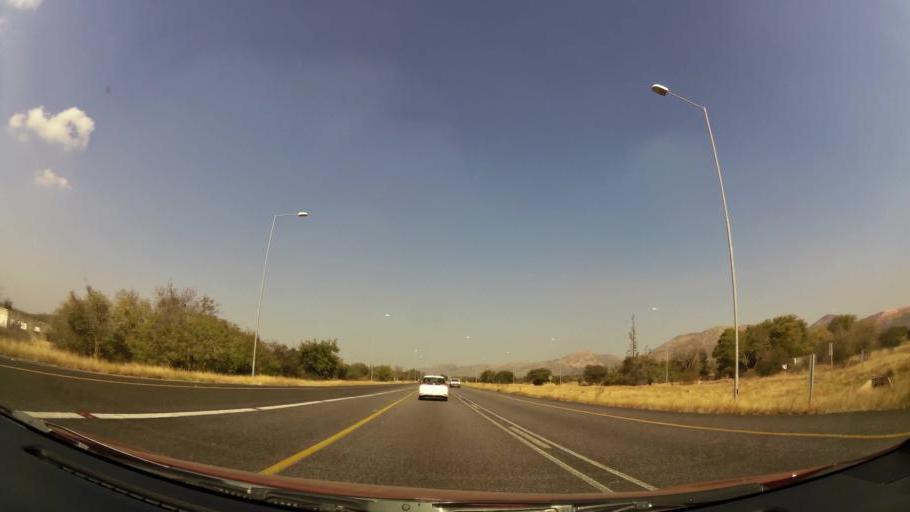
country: ZA
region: North-West
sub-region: Bojanala Platinum District Municipality
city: Rustenburg
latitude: -25.6168
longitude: 27.1545
